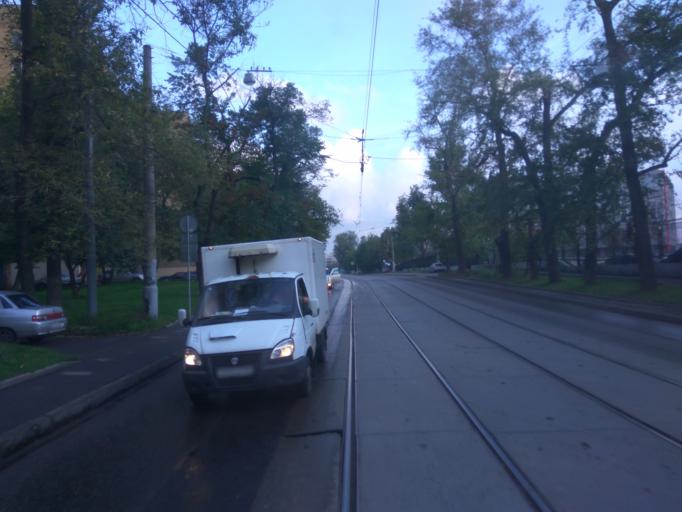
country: RU
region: Moskovskaya
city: Bogorodskoye
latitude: 55.8082
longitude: 37.7059
